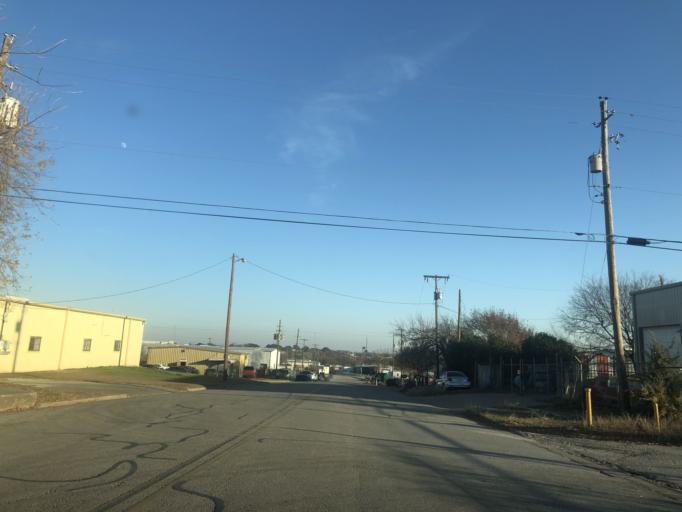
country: US
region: Texas
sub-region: Travis County
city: Wells Branch
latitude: 30.4312
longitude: -97.6828
